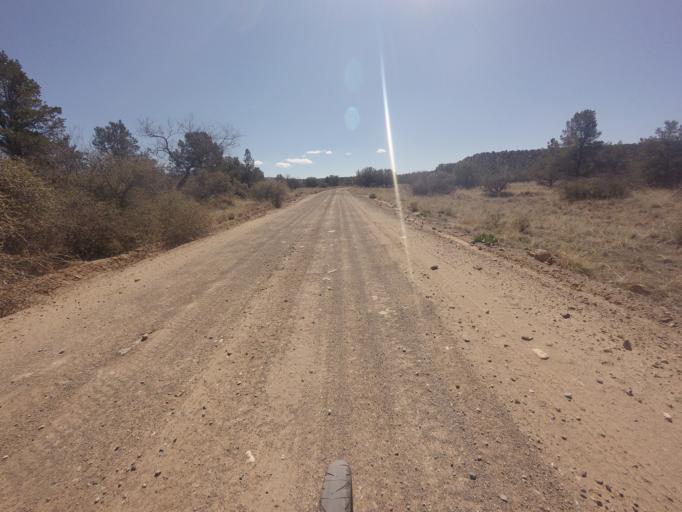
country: US
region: Arizona
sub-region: Yavapai County
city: Lake Montezuma
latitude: 34.6071
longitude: -111.7244
